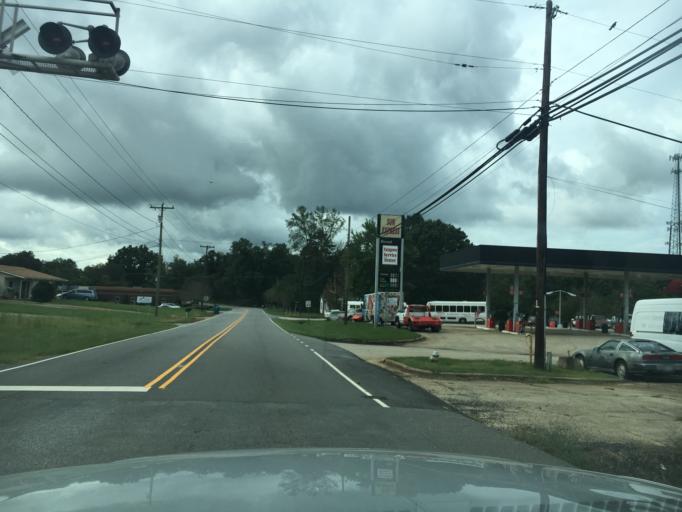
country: US
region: North Carolina
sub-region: Catawba County
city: Saint Stephens
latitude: 35.7221
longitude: -81.2646
